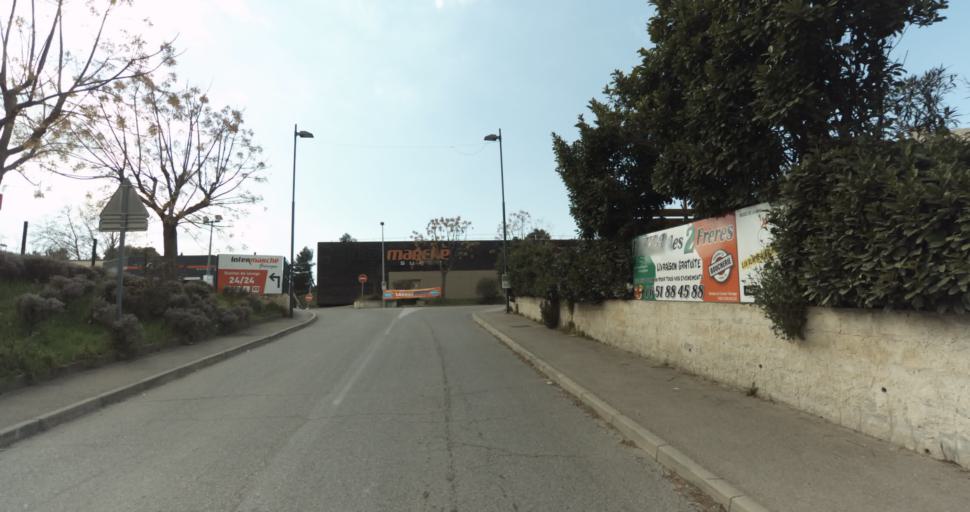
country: FR
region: Provence-Alpes-Cote d'Azur
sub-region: Departement des Bouches-du-Rhone
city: Greasque
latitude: 43.4352
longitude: 5.5409
